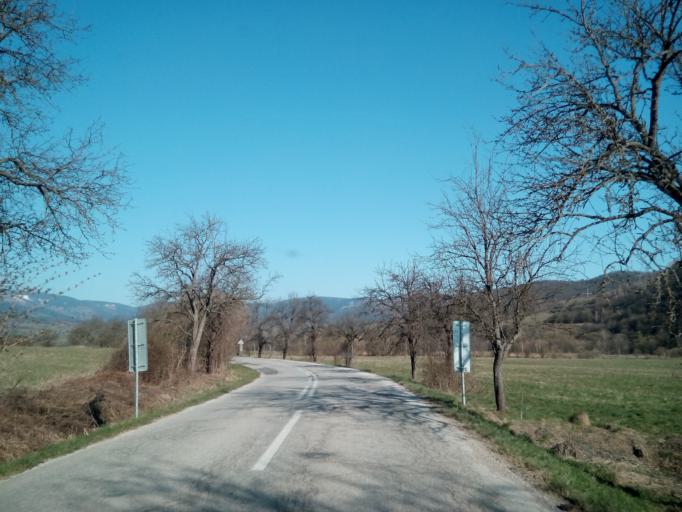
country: SK
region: Kosicky
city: Dobsina
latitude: 48.6956
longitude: 20.3137
